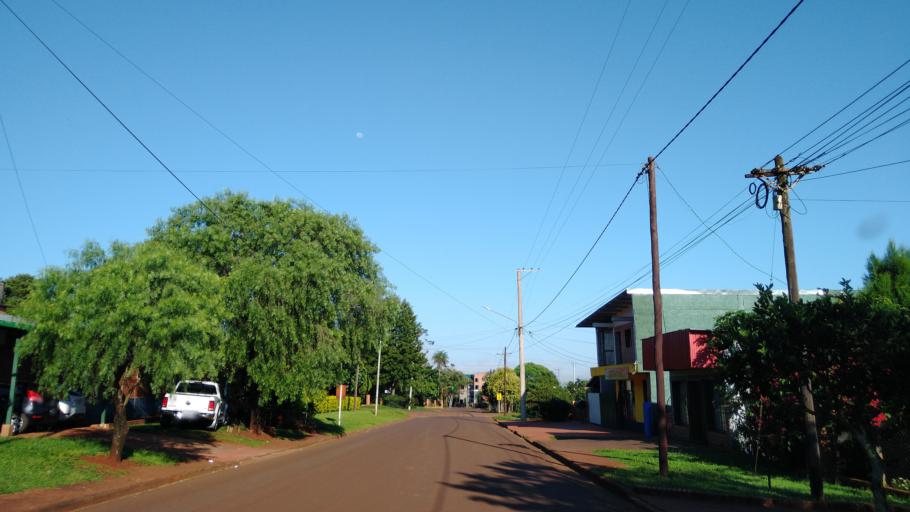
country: AR
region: Misiones
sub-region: Departamento de Montecarlo
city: Montecarlo
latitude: -26.5651
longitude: -54.7605
